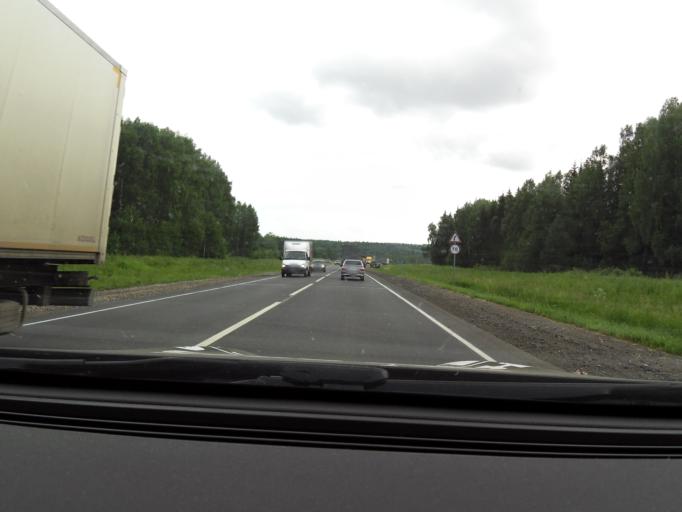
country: RU
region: Perm
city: Suksun
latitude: 57.1464
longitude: 57.2878
